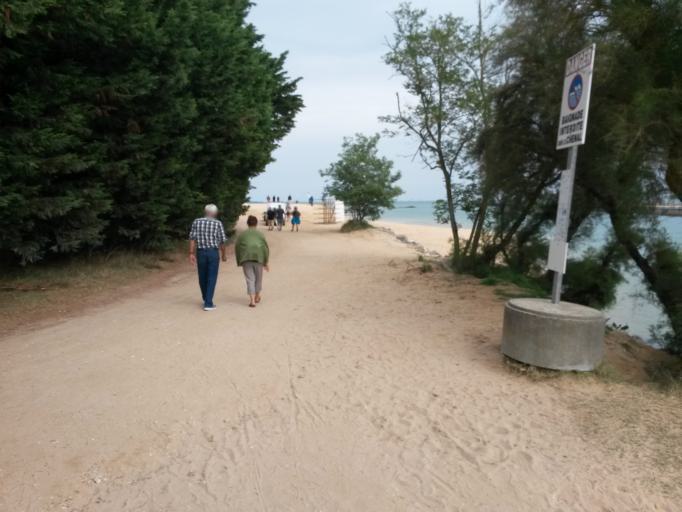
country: FR
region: Poitou-Charentes
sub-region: Departement de la Charente-Maritime
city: Boyard-Ville
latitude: 45.9693
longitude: -1.2362
